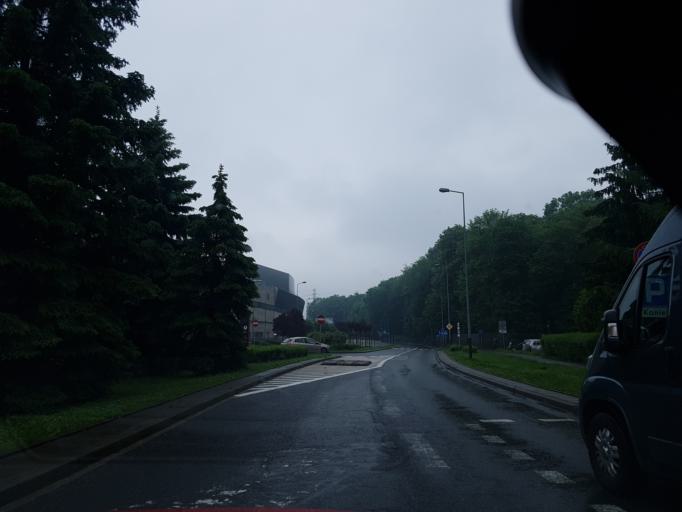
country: PL
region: Lesser Poland Voivodeship
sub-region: Krakow
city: Krakow
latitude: 50.0549
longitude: 19.9538
